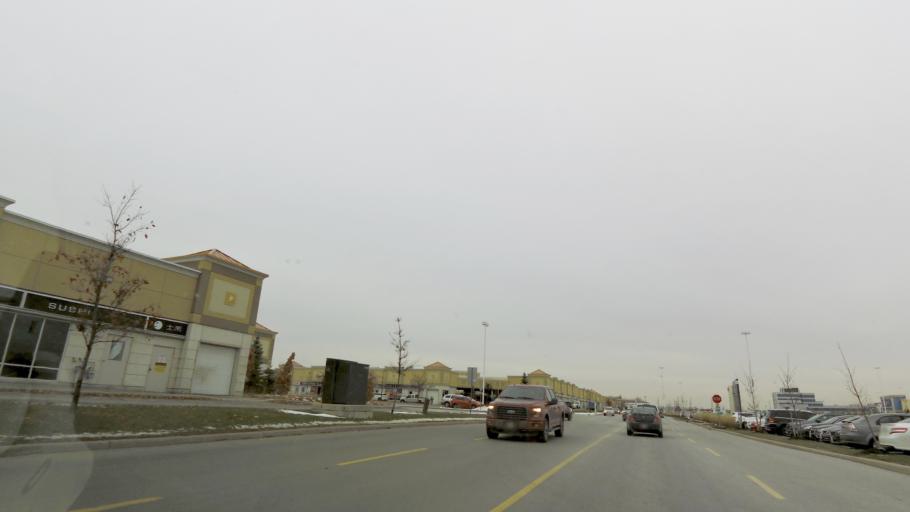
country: CA
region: Ontario
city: Vaughan
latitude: 43.8273
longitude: -79.5394
